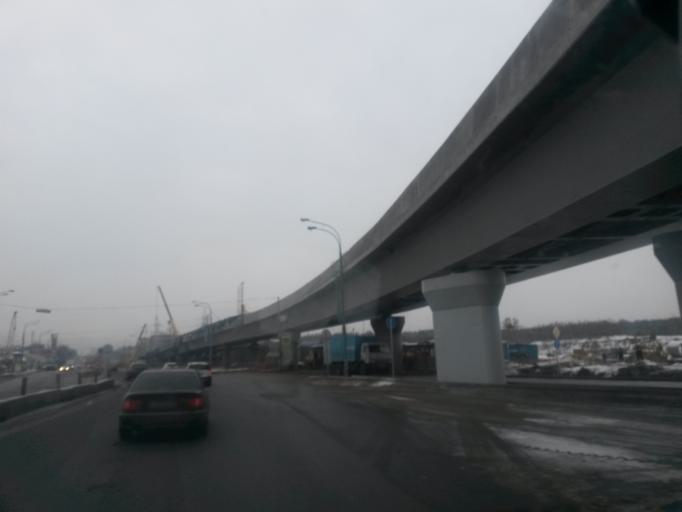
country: RU
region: Moskovskaya
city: Bol'shaya Setun'
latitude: 55.7028
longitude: 37.4204
